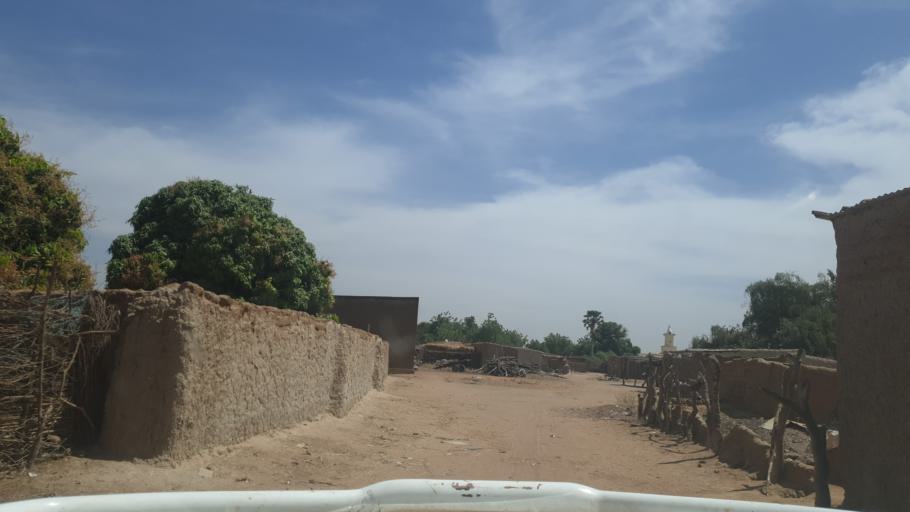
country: ML
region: Sikasso
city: Yorosso
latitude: 12.2918
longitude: -4.6509
